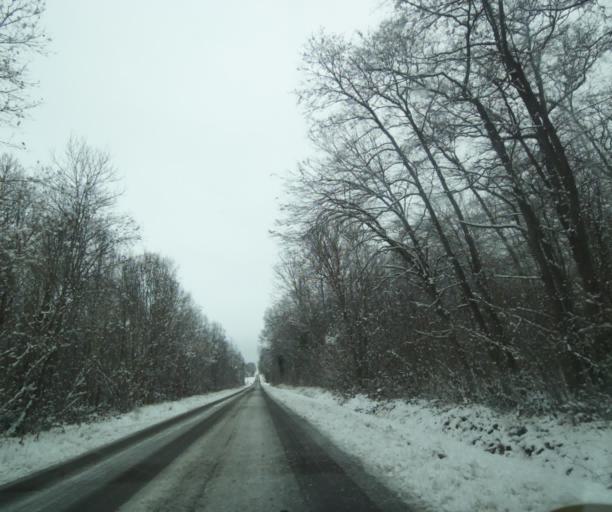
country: FR
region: Champagne-Ardenne
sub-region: Departement de la Haute-Marne
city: Montier-en-Der
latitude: 48.5208
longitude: 4.7477
